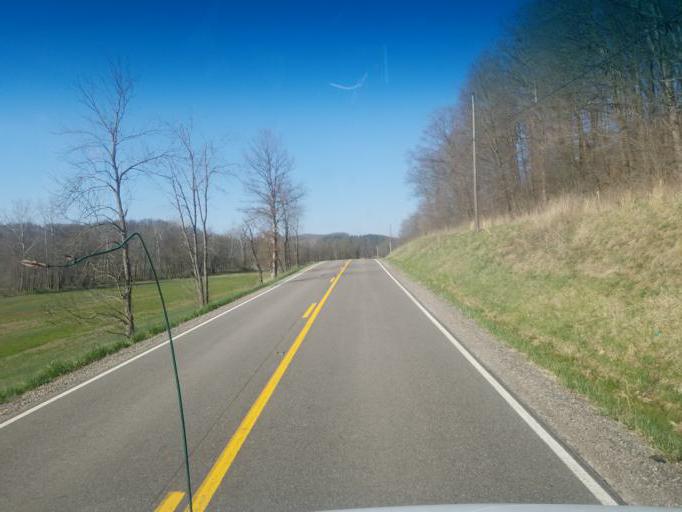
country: US
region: Ohio
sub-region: Muskingum County
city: Frazeysburg
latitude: 40.2193
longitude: -82.1709
